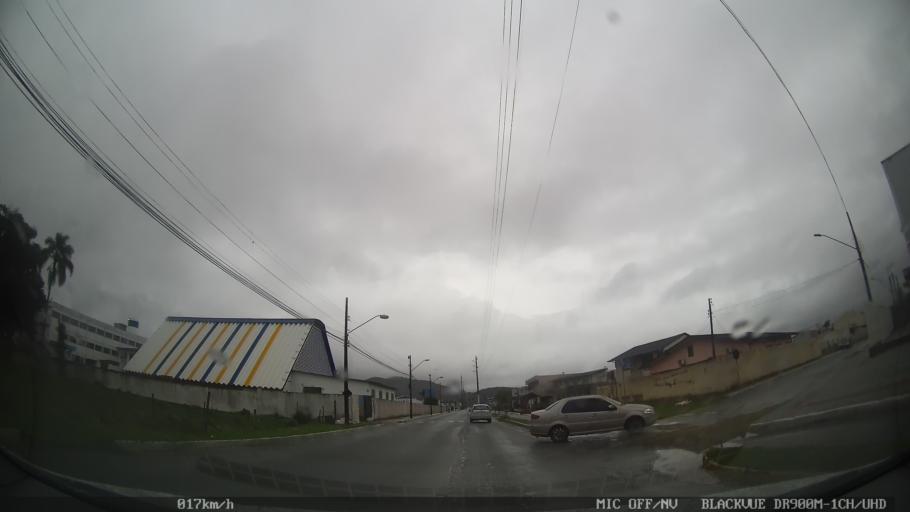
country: BR
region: Santa Catarina
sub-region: Itajai
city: Itajai
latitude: -26.9199
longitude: -48.6992
